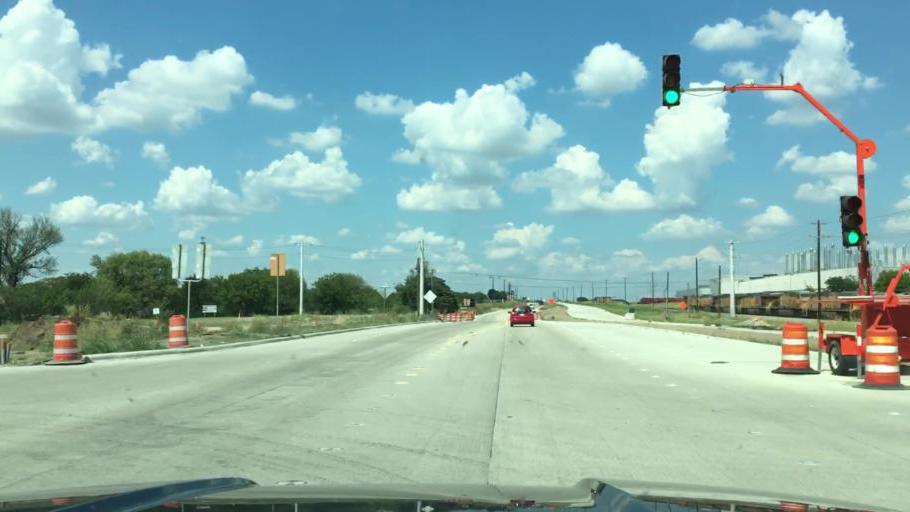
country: US
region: Texas
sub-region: Denton County
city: Justin
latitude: 33.0301
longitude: -97.3093
